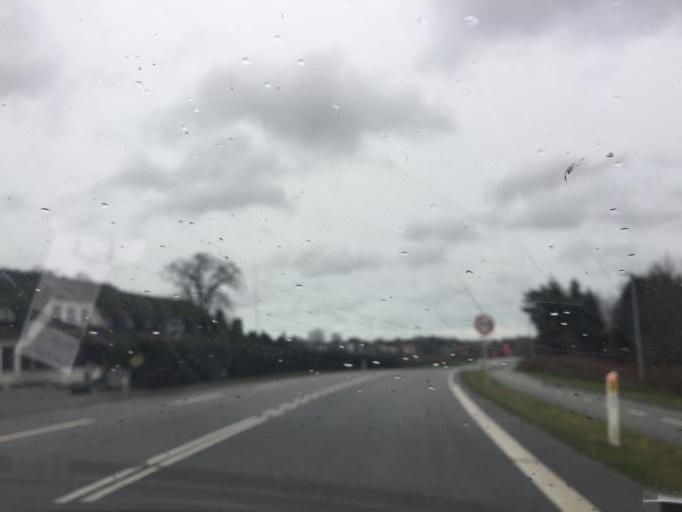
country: DK
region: South Denmark
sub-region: Fredericia Kommune
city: Taulov
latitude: 55.5336
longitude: 9.5988
